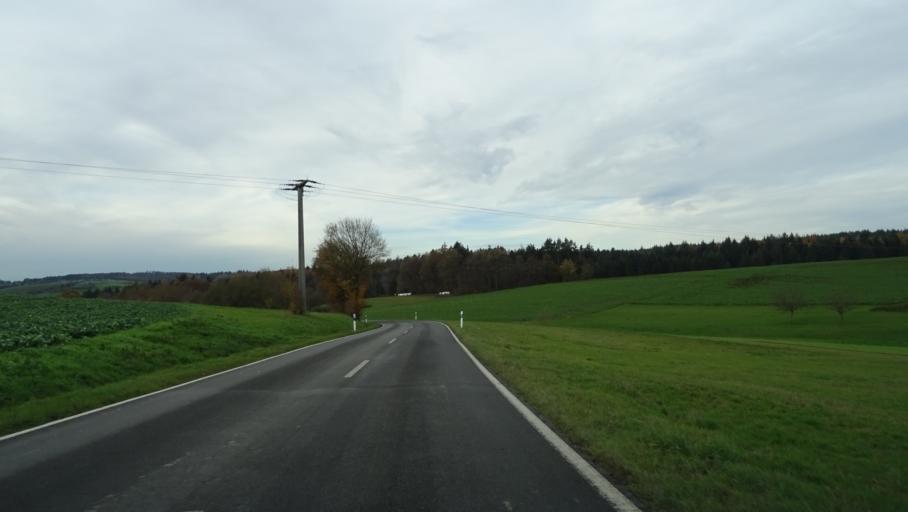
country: DE
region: Baden-Wuerttemberg
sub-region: Karlsruhe Region
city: Fahrenbach
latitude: 49.4059
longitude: 9.1547
